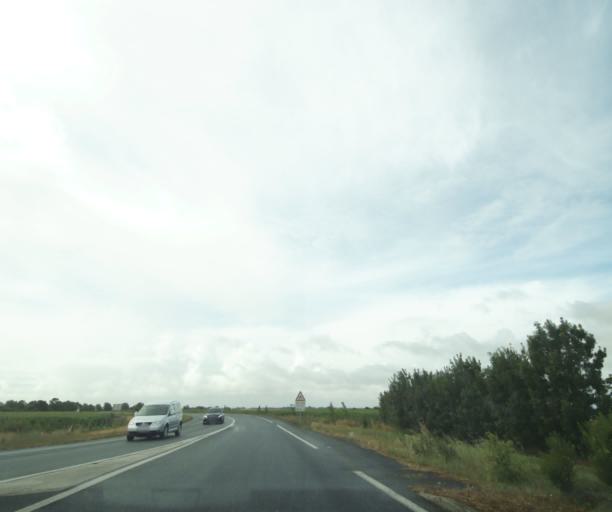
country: FR
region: Pays de la Loire
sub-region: Departement de la Vendee
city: Champagne-les-Marais
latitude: 46.3745
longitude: -1.0921
